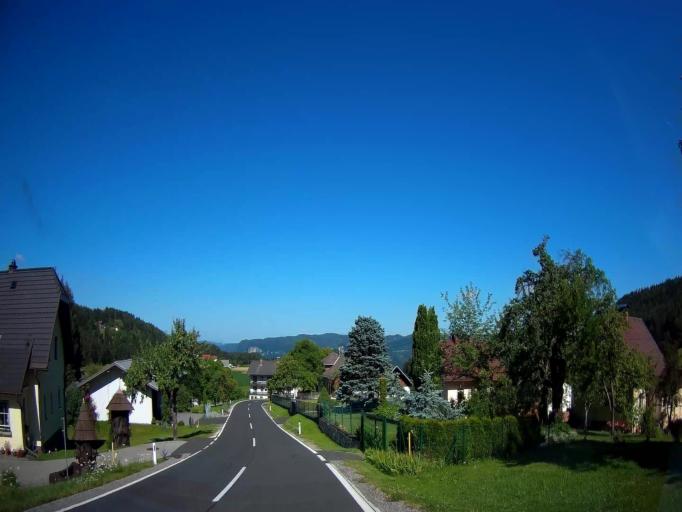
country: AT
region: Carinthia
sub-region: Politischer Bezirk Klagenfurt Land
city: Grafenstein
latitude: 46.5382
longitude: 14.4474
